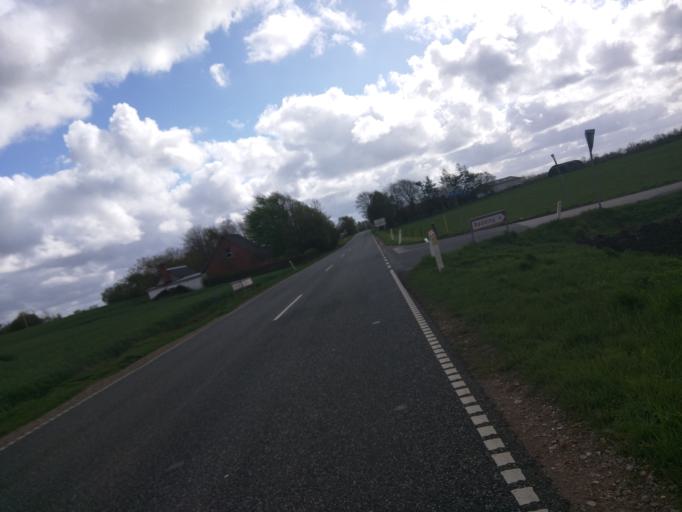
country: DK
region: Central Jutland
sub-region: Viborg Kommune
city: Bjerringbro
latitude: 56.4763
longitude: 9.5581
